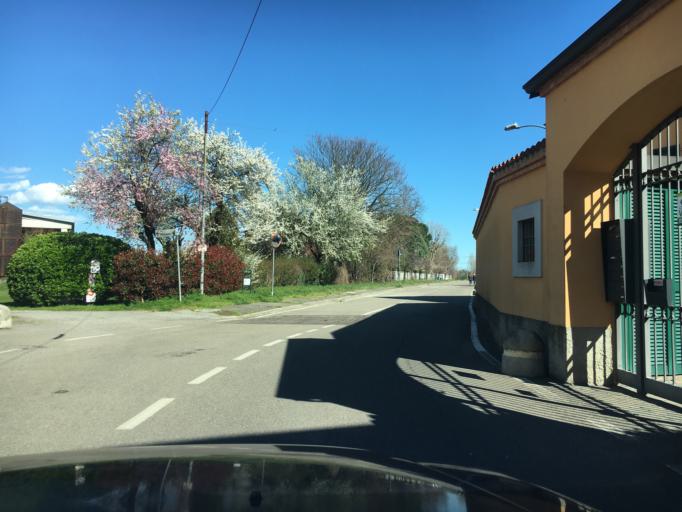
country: IT
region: Lombardy
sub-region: Citta metropolitana di Milano
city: Cusago
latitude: 45.4591
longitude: 9.0428
